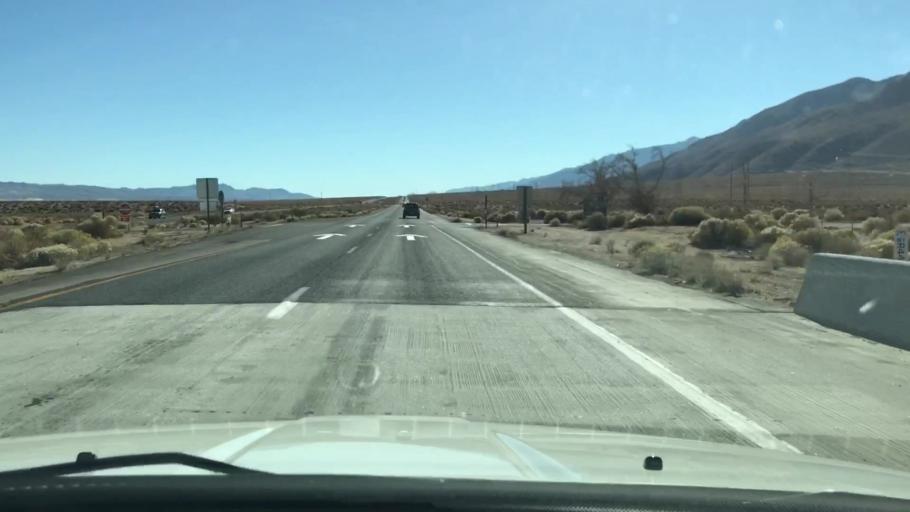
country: US
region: California
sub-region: Inyo County
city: Lone Pine
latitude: 36.4114
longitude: -118.0281
